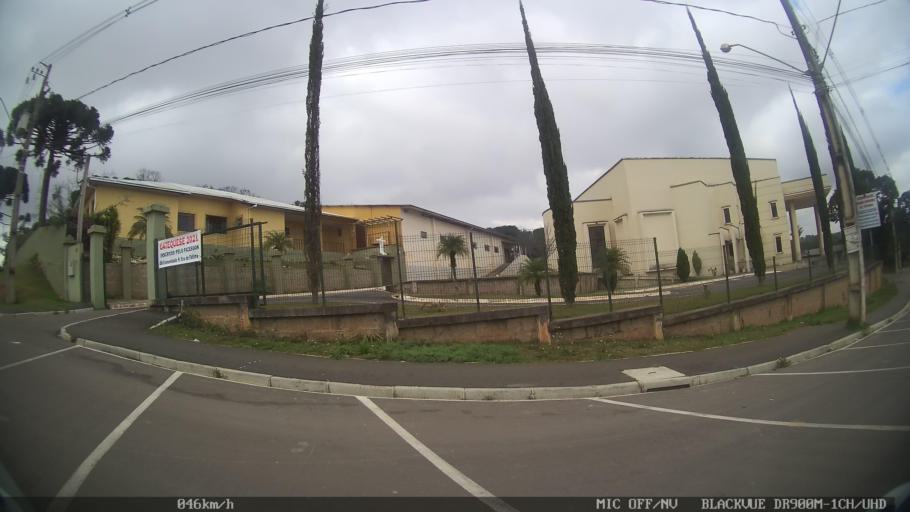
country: BR
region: Parana
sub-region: Colombo
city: Colombo
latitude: -25.3475
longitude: -49.2247
